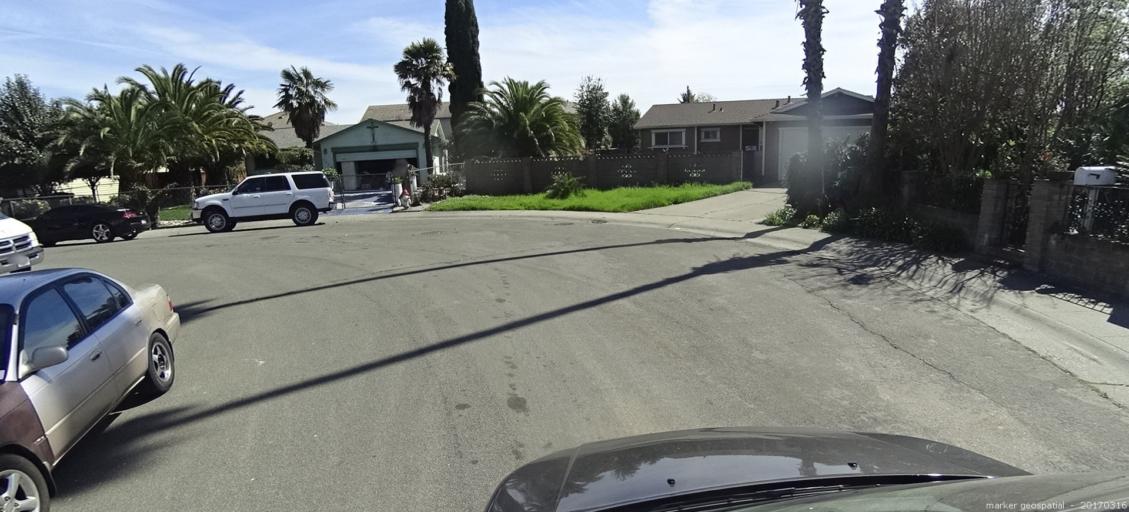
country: US
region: California
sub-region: Sacramento County
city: Parkway
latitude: 38.4743
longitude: -121.5012
